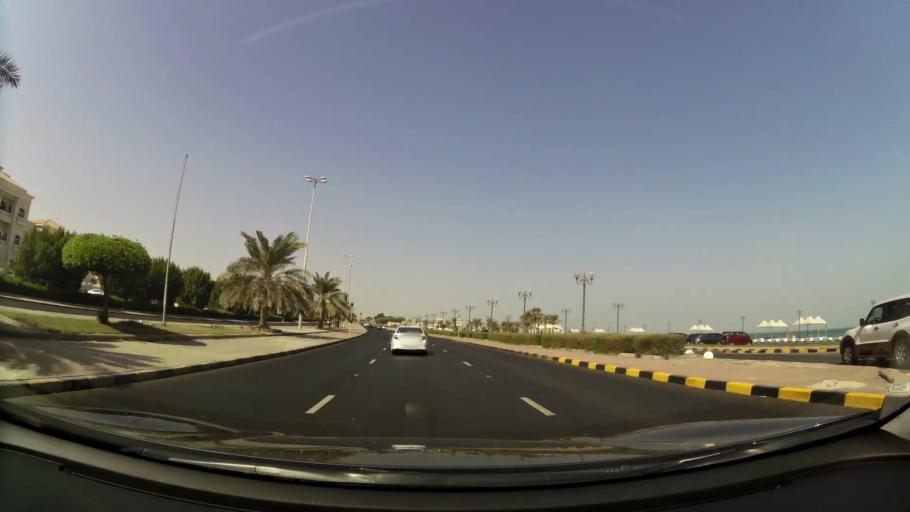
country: KW
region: Muhafazat Hawalli
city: Salwa
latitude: 29.2747
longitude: 48.0890
